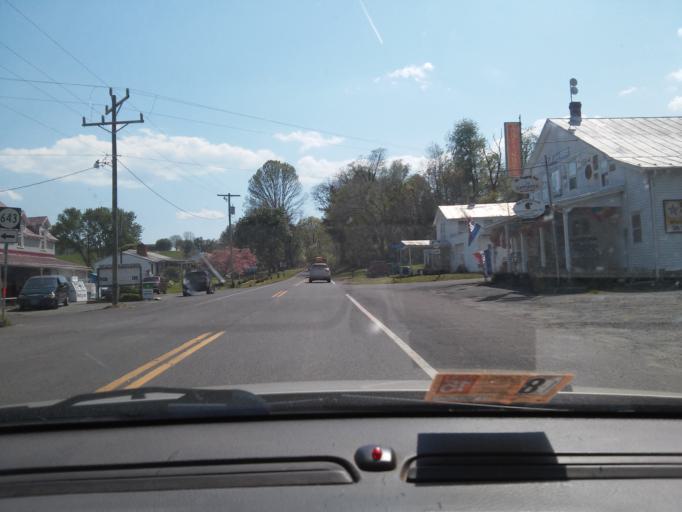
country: US
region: Virginia
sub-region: Madison County
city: Brightwood
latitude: 38.5258
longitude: -78.2621
